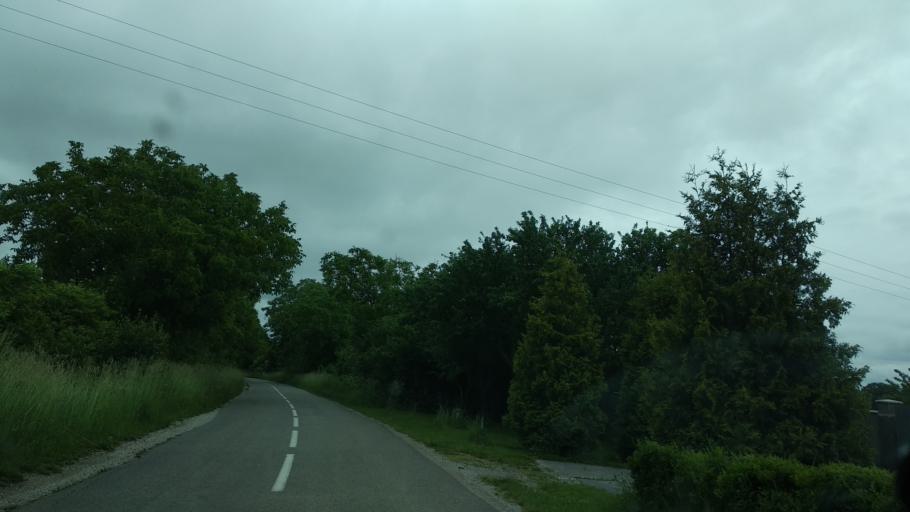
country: SK
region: Nitriansky
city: Trencianske Teplice
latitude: 48.7897
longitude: 18.1377
